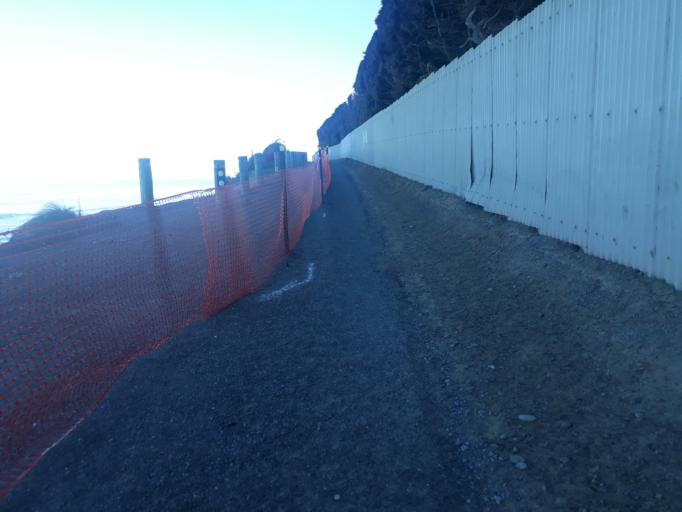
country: NZ
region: Canterbury
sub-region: Timaru District
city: Timaru
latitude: -44.4136
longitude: 171.2647
